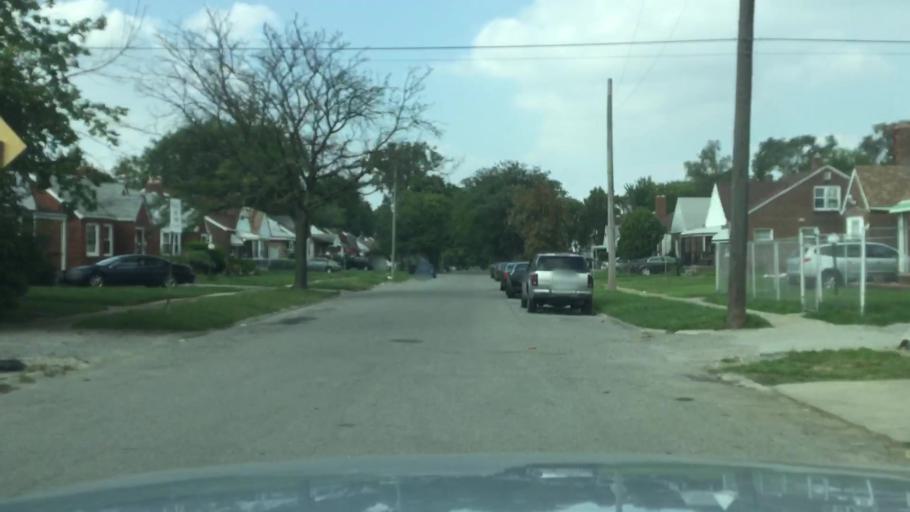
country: US
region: Michigan
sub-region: Wayne County
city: Dearborn
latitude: 42.3585
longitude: -83.1927
